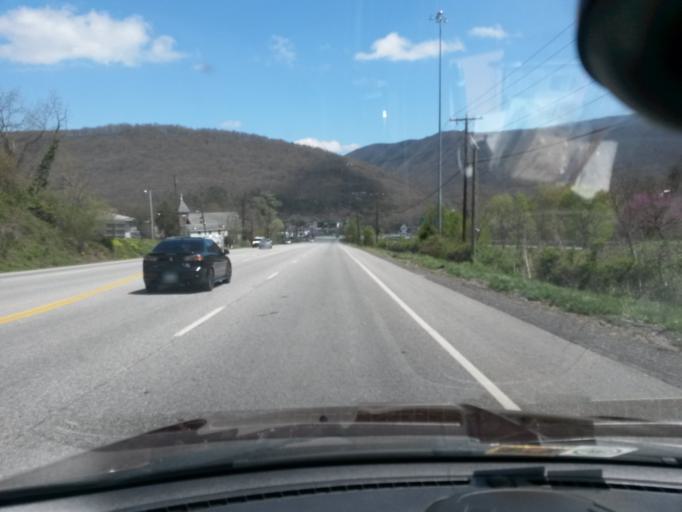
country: US
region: Virginia
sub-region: City of Covington
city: Fairlawn
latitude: 37.7776
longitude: -79.9745
